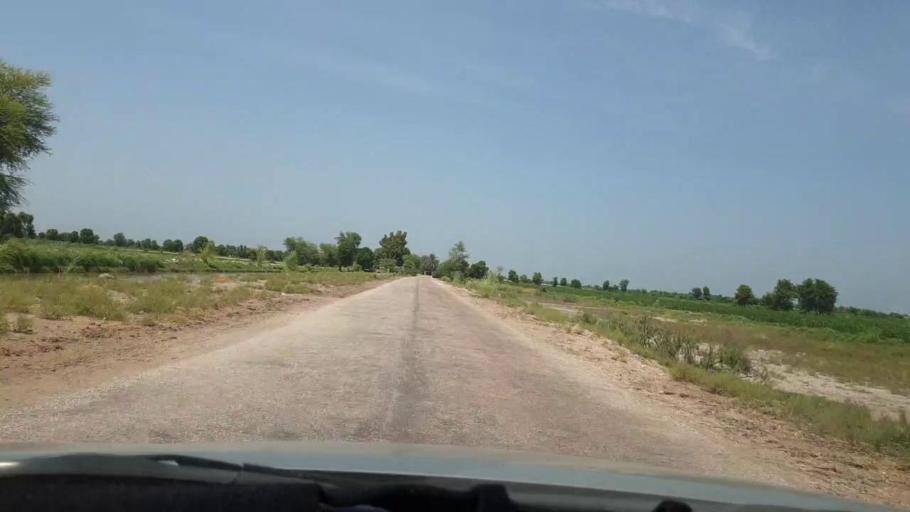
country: PK
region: Sindh
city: Pano Aqil
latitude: 27.6662
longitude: 69.1081
